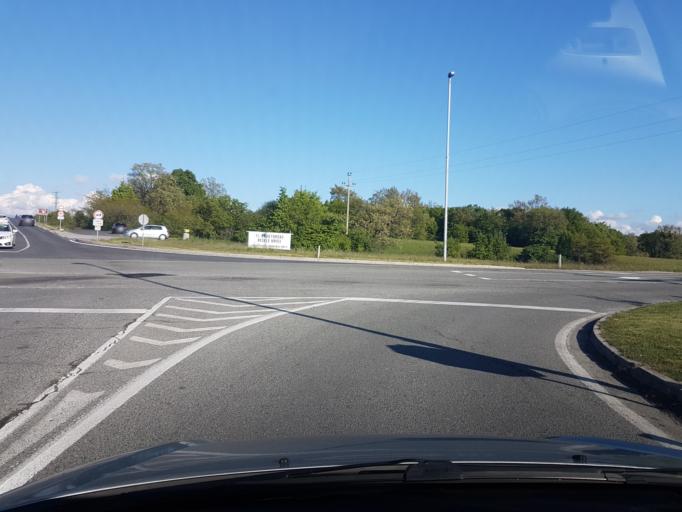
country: SI
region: Divaca
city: Divaca
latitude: 45.6794
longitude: 13.9714
